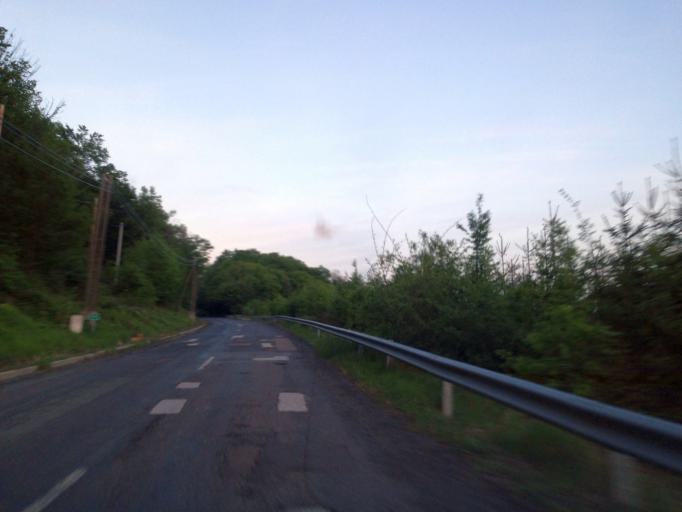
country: HU
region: Nograd
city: Batonyterenye
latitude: 47.8949
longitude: 19.8644
